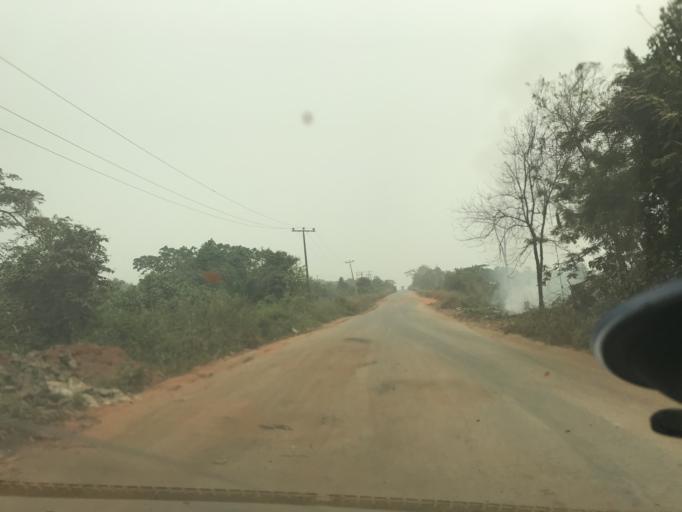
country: NG
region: Ogun
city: Owode
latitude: 6.8936
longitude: 3.5617
